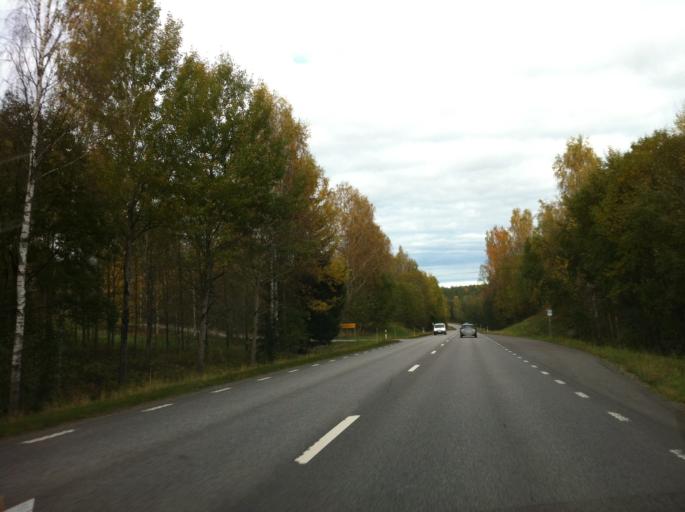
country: SE
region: OErebro
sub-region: Askersunds Kommun
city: Askersund
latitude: 58.9146
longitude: 14.9771
